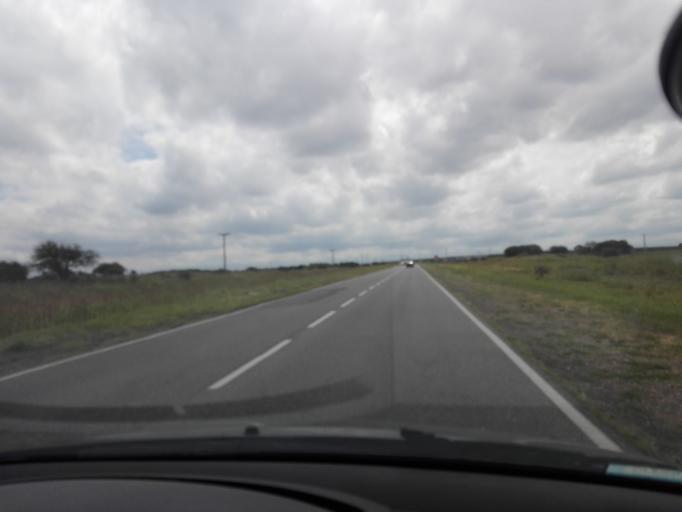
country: AR
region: Cordoba
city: Alta Gracia
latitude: -31.6521
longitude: -64.3063
